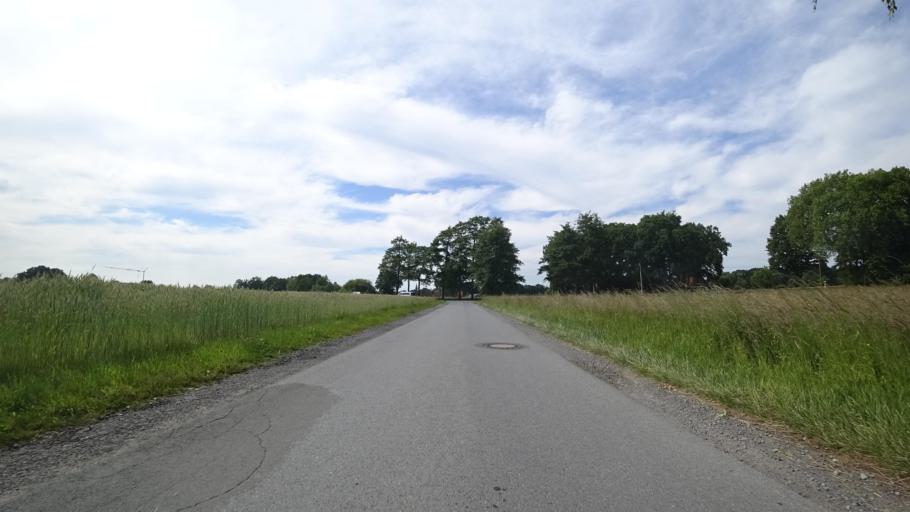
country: DE
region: North Rhine-Westphalia
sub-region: Regierungsbezirk Detmold
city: Guetersloh
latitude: 51.9061
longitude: 8.4458
